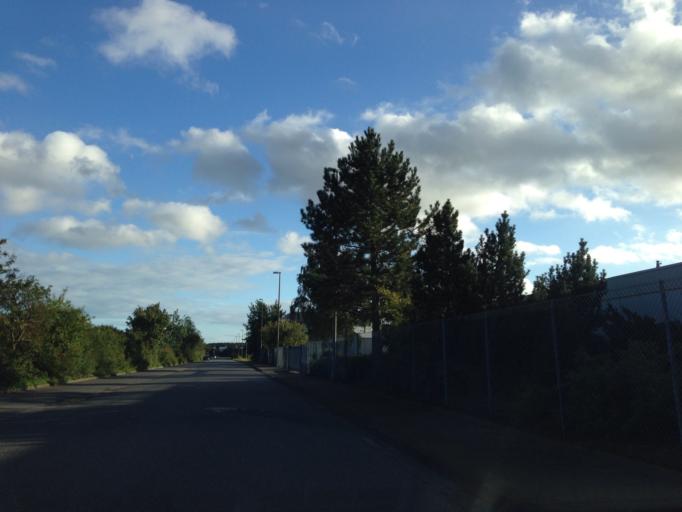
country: DE
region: Lower Saxony
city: Wendisch Evern
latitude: 53.2442
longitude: 10.4858
